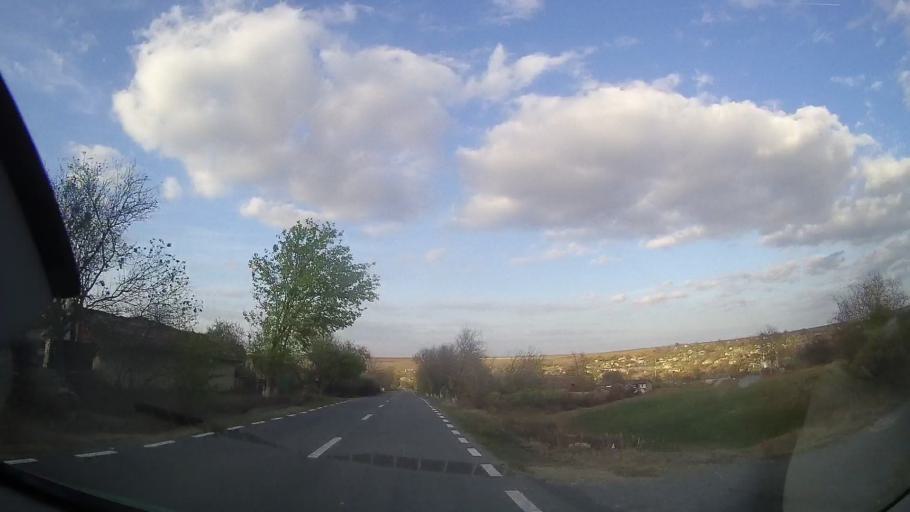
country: RO
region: Constanta
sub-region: Comuna Independenta
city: Independenta
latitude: 43.9505
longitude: 28.0749
